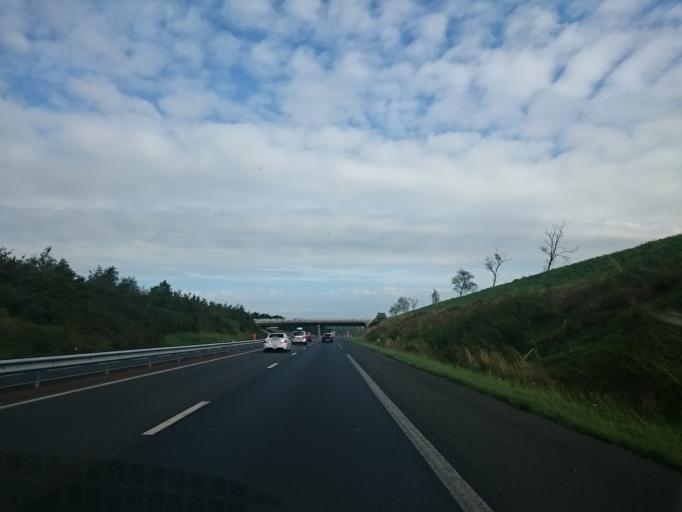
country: FR
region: Lower Normandy
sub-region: Departement de la Manche
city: Saint-Quentin-sur-le-Homme
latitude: 48.6281
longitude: -1.3393
